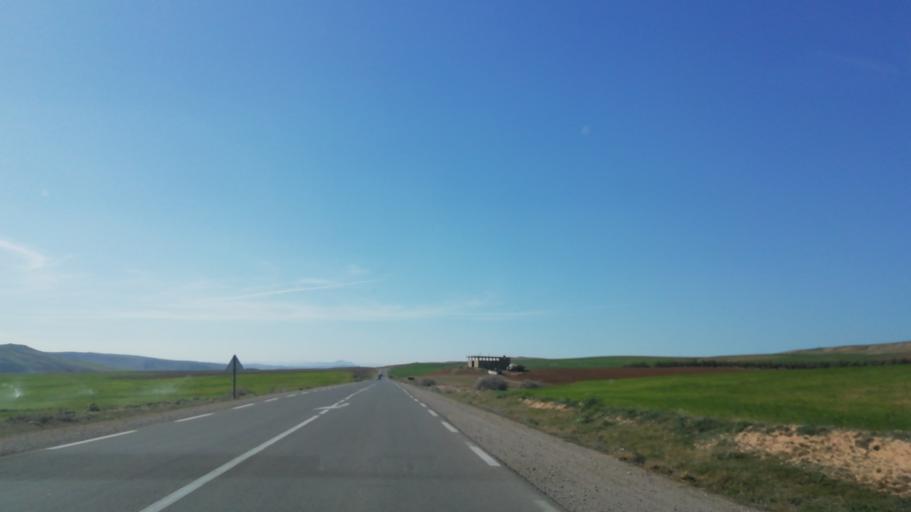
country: DZ
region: Mascara
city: Oued el Abtal
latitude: 35.4449
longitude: 0.8255
